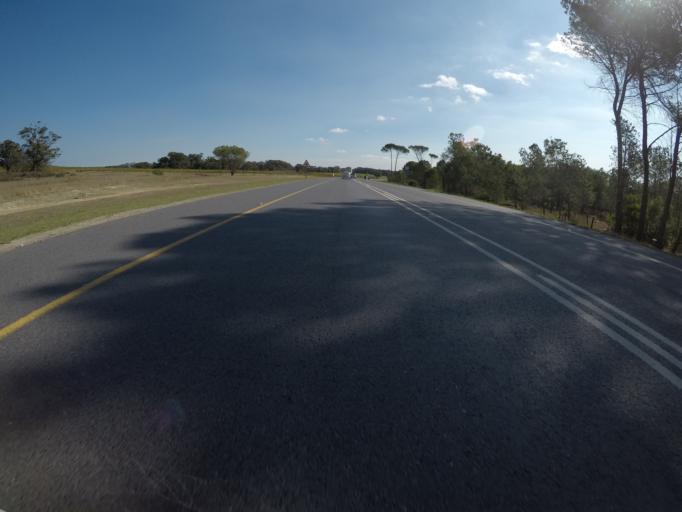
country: ZA
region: Western Cape
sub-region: City of Cape Town
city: Kraaifontein
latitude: -33.8793
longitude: 18.7658
